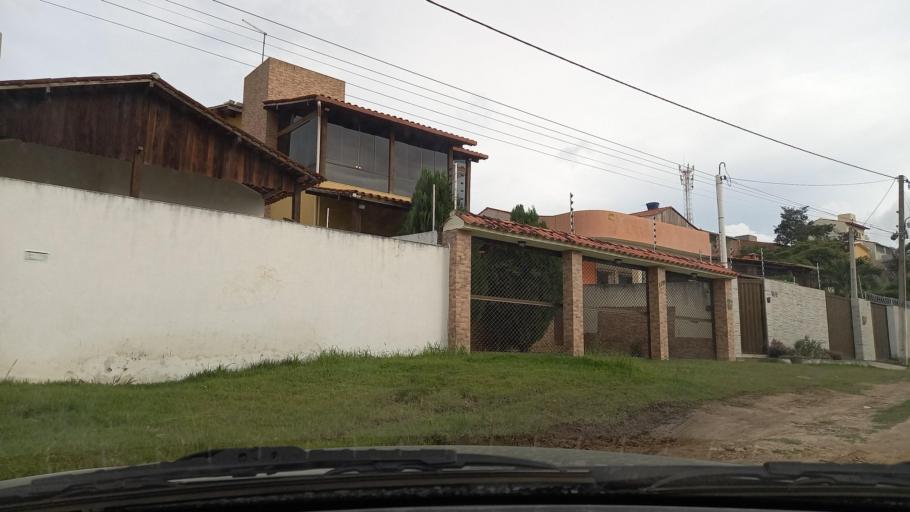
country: BR
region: Pernambuco
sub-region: Gravata
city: Gravata
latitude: -8.2025
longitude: -35.5464
